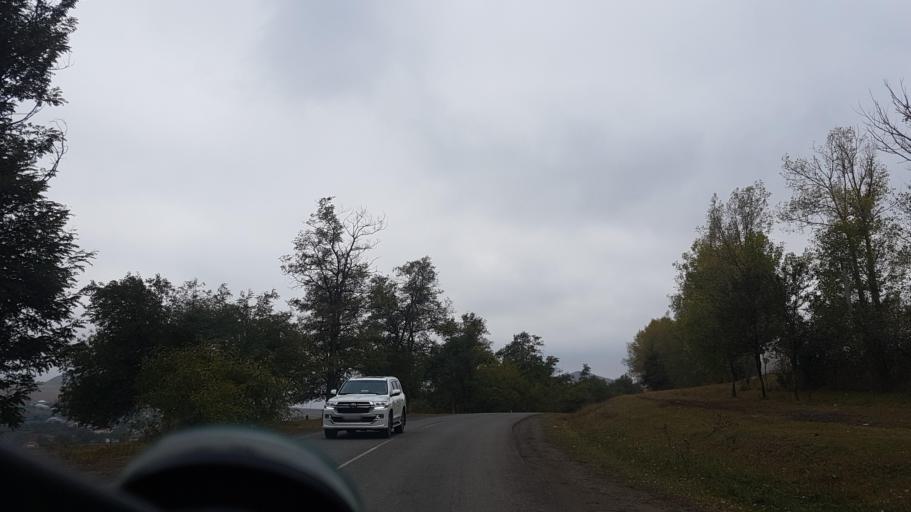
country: AZ
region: Gadabay Rayon
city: Ariqdam
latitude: 40.6460
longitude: 45.8125
